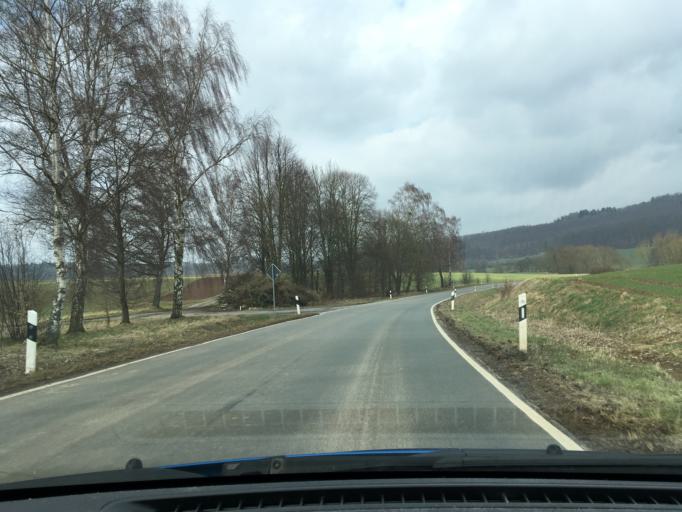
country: DE
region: Lower Saxony
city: Adelebsen
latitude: 51.5444
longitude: 9.7388
